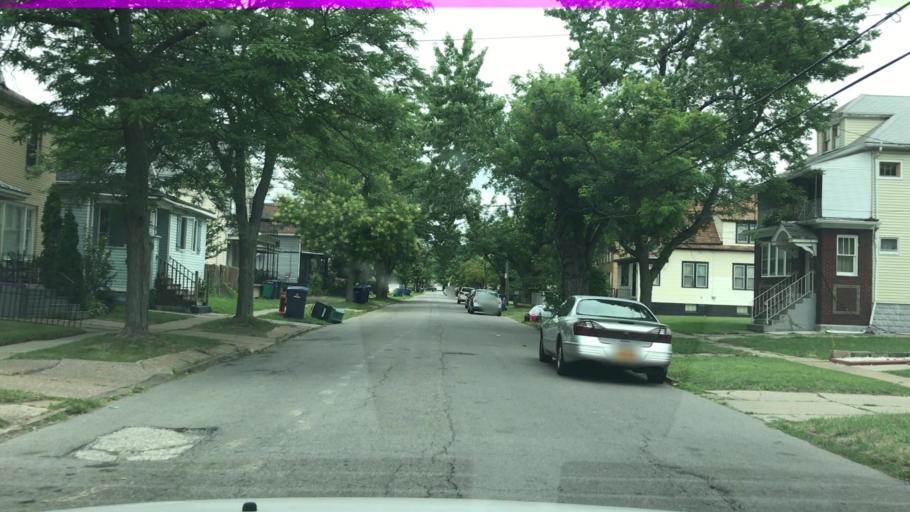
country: US
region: New York
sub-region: Erie County
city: Sloan
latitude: 42.9246
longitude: -78.8034
